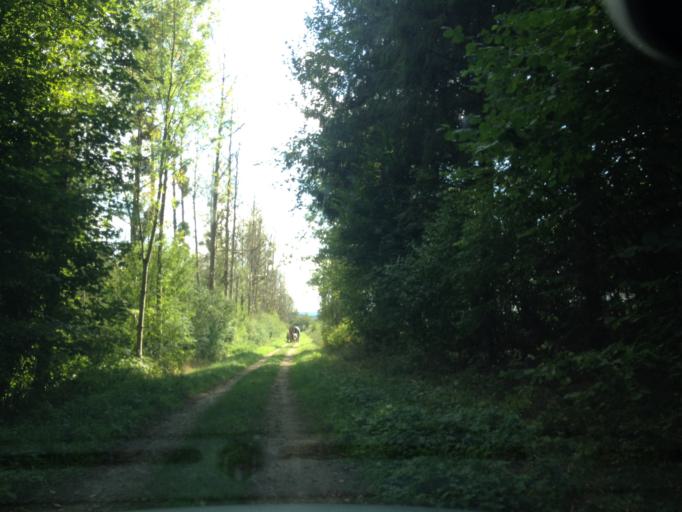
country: FR
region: Franche-Comte
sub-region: Departement de la Haute-Saone
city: Saint-Loup-sur-Semouse
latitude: 47.8276
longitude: 6.2096
